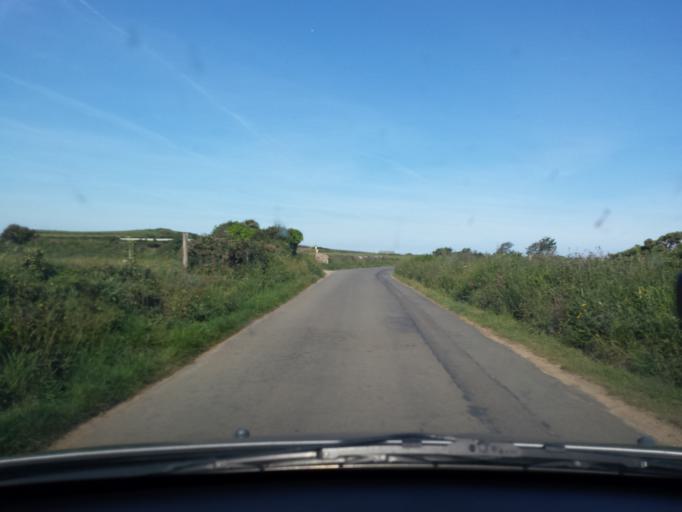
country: FR
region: Lower Normandy
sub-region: Departement de la Manche
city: Beaumont-Hague
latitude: 49.6761
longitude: -1.9310
